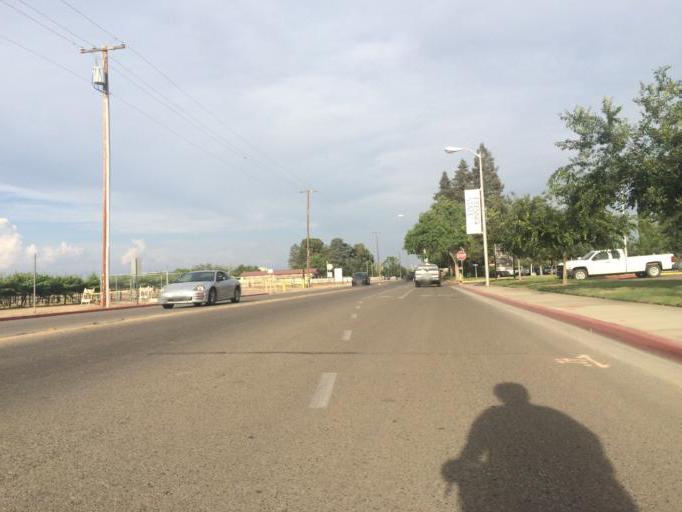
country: US
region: California
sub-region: Fresno County
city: Clovis
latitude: 36.8158
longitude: -119.7460
